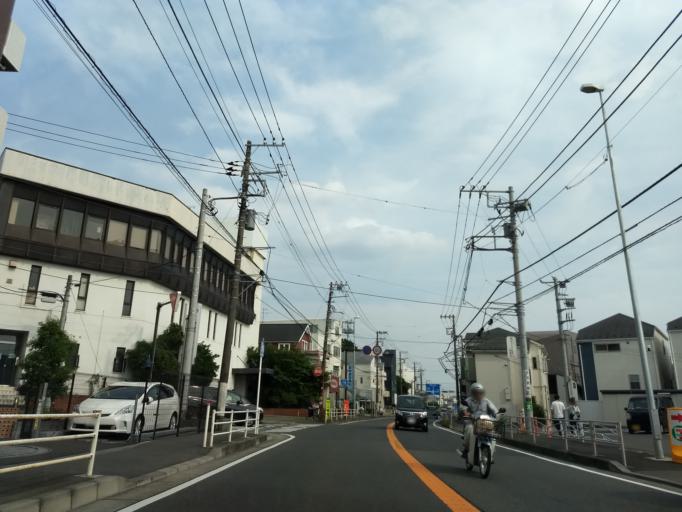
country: JP
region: Kanagawa
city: Yokohama
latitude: 35.4772
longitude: 139.5711
